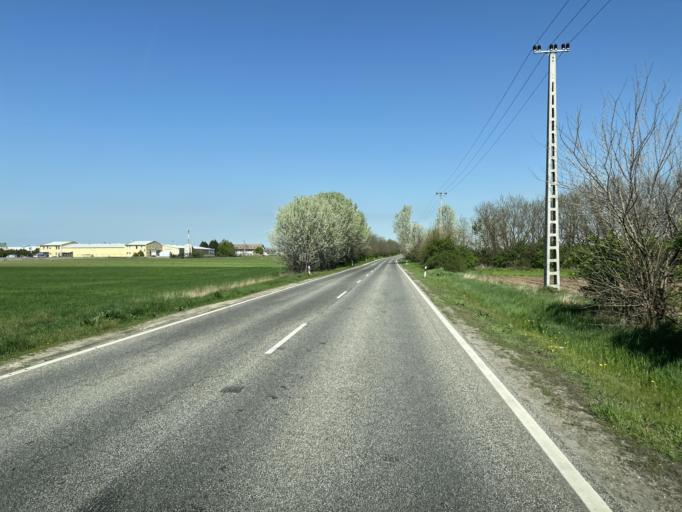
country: HU
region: Pest
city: Alsonemedi
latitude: 47.3462
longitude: 19.1684
